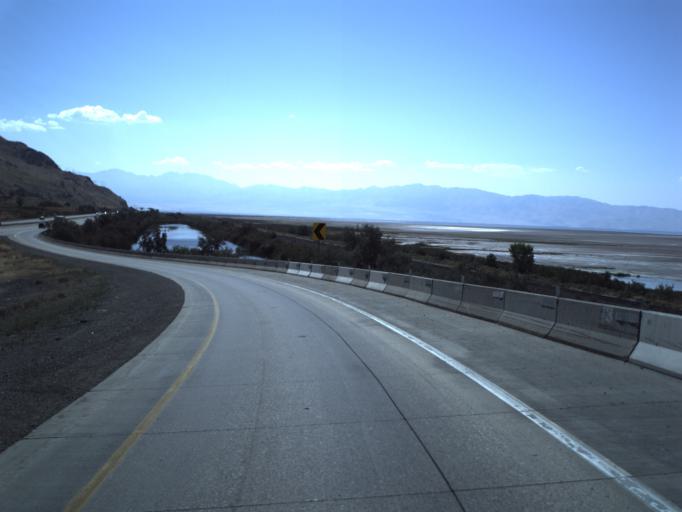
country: US
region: Utah
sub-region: Tooele County
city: Stansbury park
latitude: 40.7227
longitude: -112.2280
